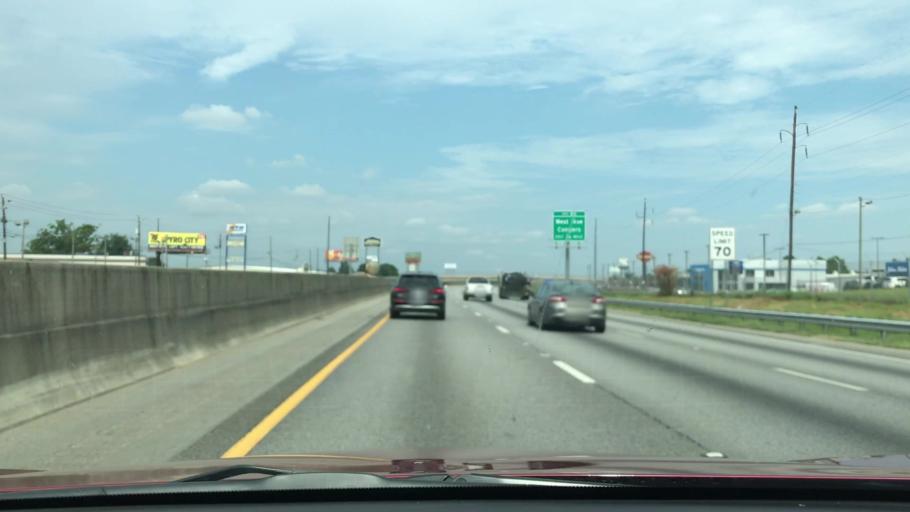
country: US
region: Georgia
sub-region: Rockdale County
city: Conyers
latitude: 33.6564
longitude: -84.0149
